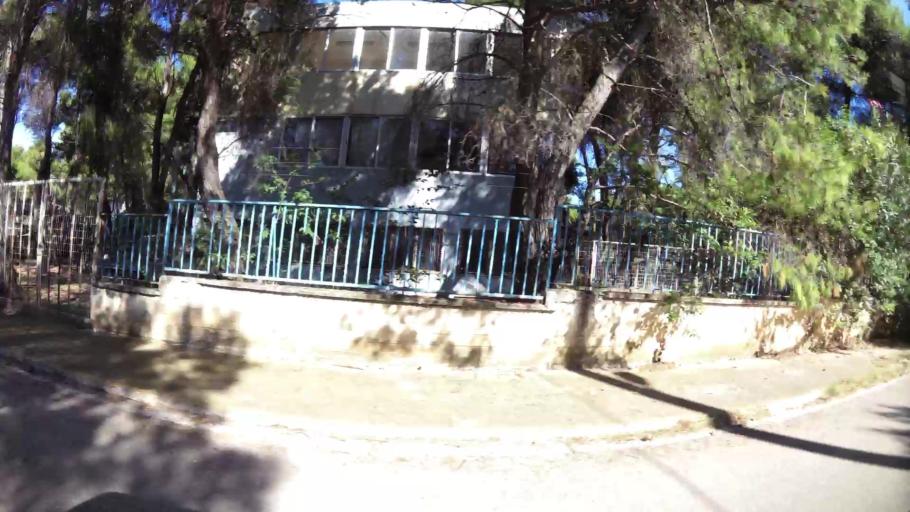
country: GR
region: Attica
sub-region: Nomarchia Athinas
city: Ekali
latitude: 38.1079
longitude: 23.8271
